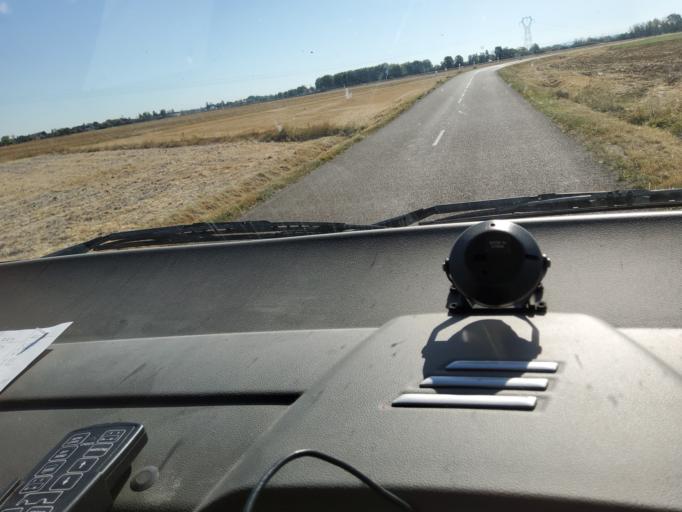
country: FR
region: Bourgogne
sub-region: Departement de la Cote-d'Or
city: Saint-Usage
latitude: 47.1398
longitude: 5.2606
